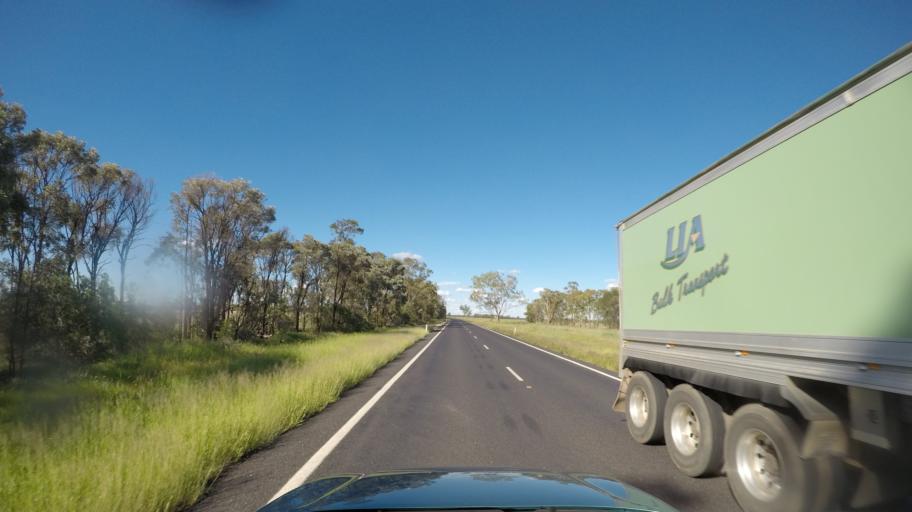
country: AU
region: Queensland
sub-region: Goondiwindi
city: Goondiwindi
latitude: -28.1410
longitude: 150.6912
